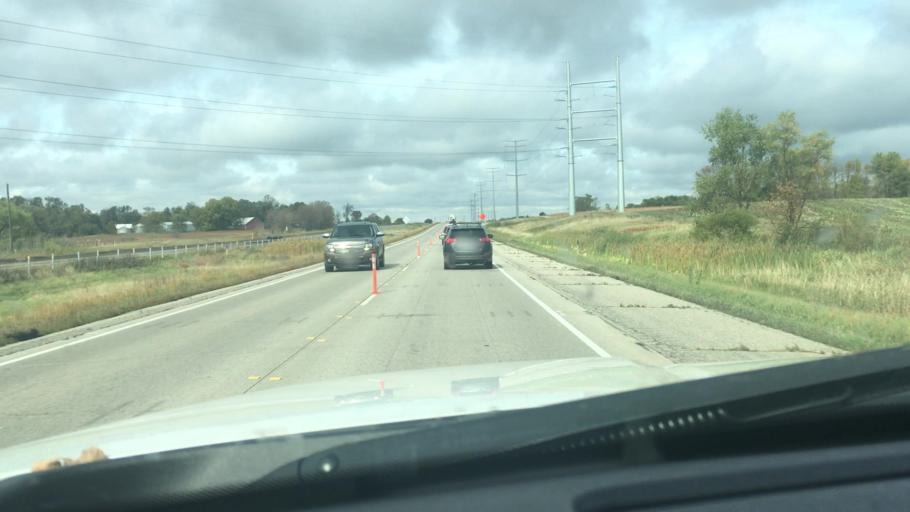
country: US
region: Minnesota
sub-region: Douglas County
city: Alexandria
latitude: 45.9189
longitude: -95.5567
